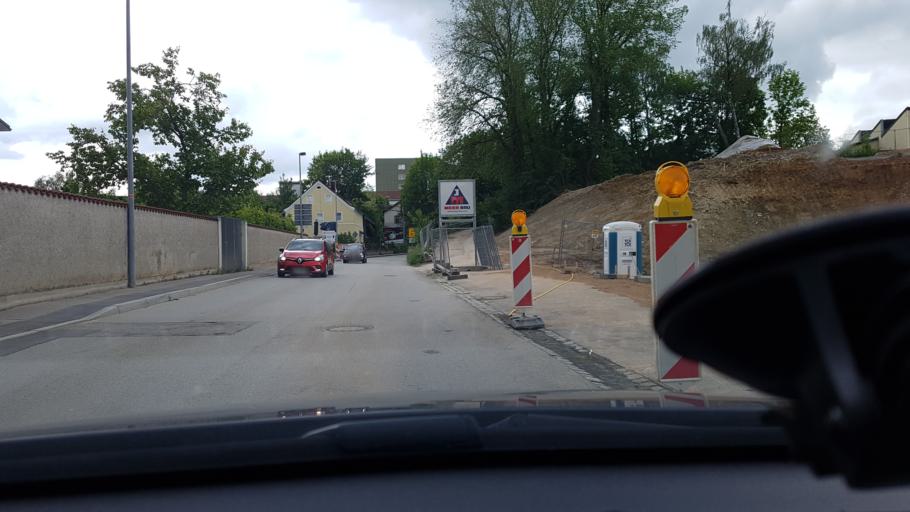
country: DE
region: Bavaria
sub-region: Lower Bavaria
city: Rotthalmunster
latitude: 48.3571
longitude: 13.2021
